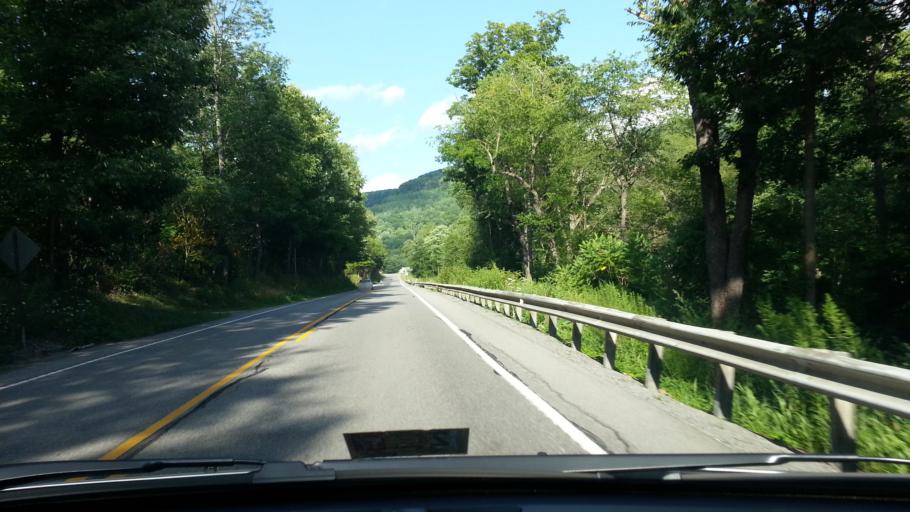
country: US
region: Pennsylvania
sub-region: Elk County
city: Saint Marys
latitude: 41.2523
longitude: -78.5137
